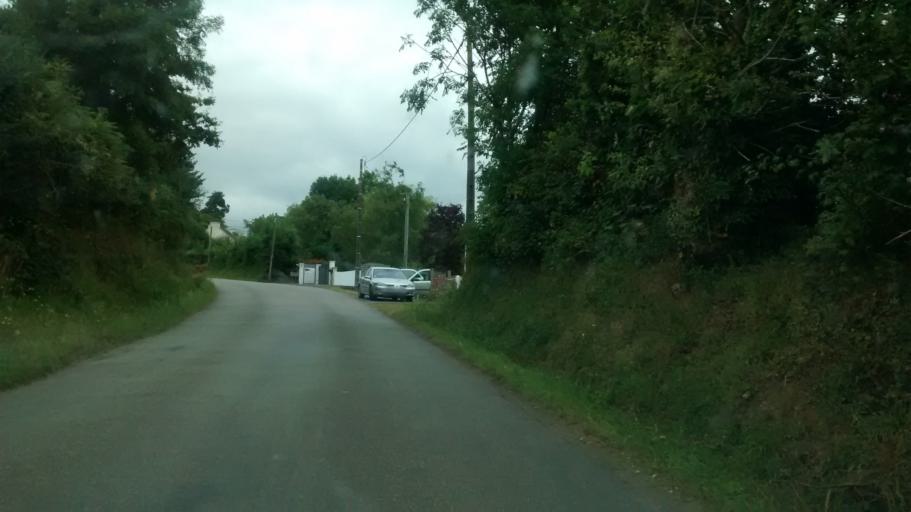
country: FR
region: Brittany
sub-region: Departement du Finistere
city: Plougastel-Daoulas
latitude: 48.3531
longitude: -4.3898
